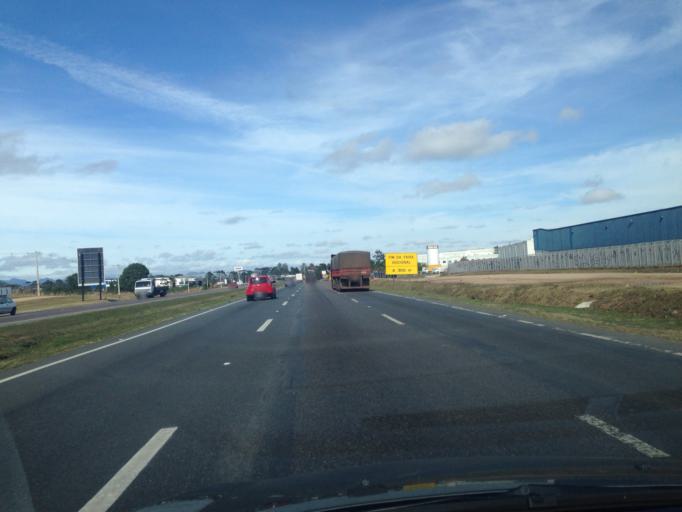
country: BR
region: Parana
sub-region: Sao Jose Dos Pinhais
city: Sao Jose dos Pinhais
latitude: -25.5479
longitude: -49.1505
